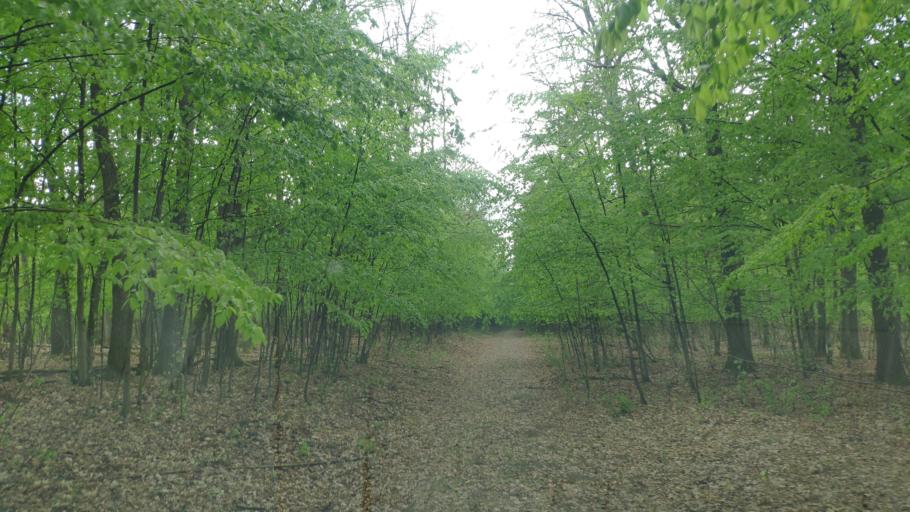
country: SK
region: Kosicky
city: Moldava nad Bodvou
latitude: 48.5469
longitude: 20.9306
